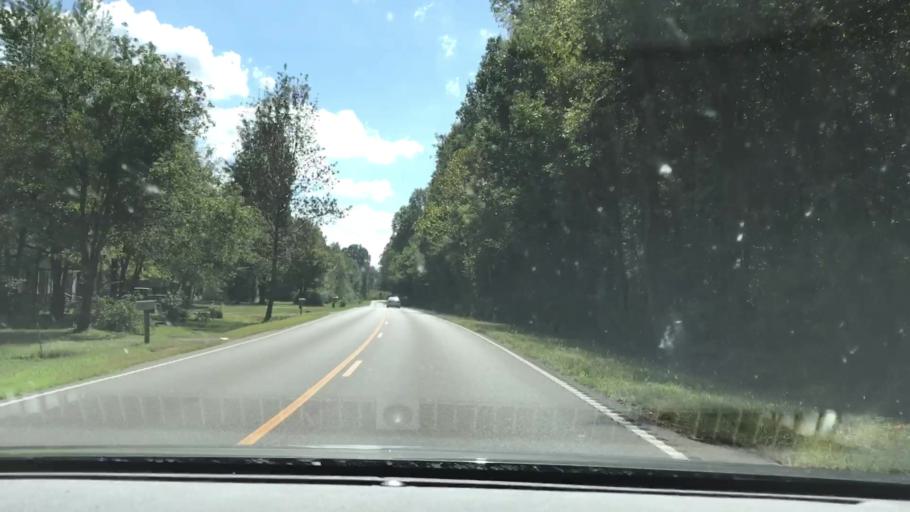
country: US
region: Kentucky
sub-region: McCracken County
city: Reidland
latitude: 36.9673
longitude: -88.5153
